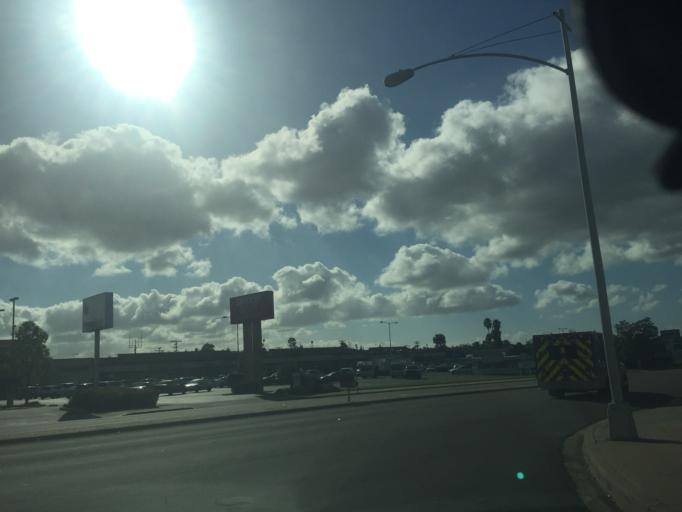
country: US
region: California
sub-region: San Diego County
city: La Mesa
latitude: 32.7926
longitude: -117.0810
